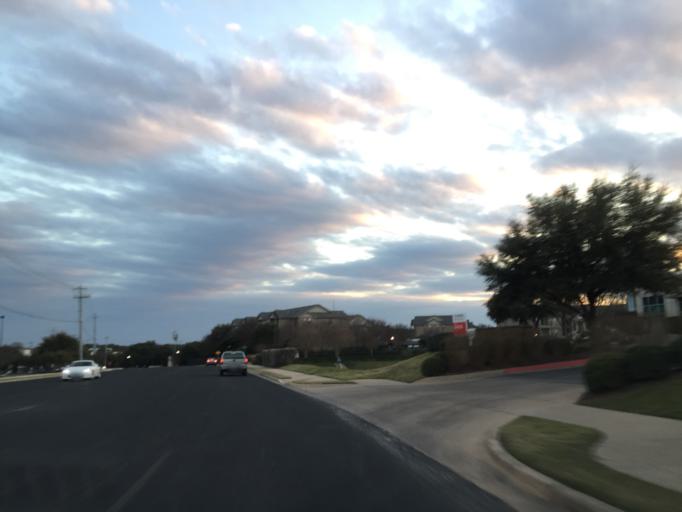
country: US
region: Texas
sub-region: Williamson County
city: Jollyville
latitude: 30.4341
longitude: -97.7389
